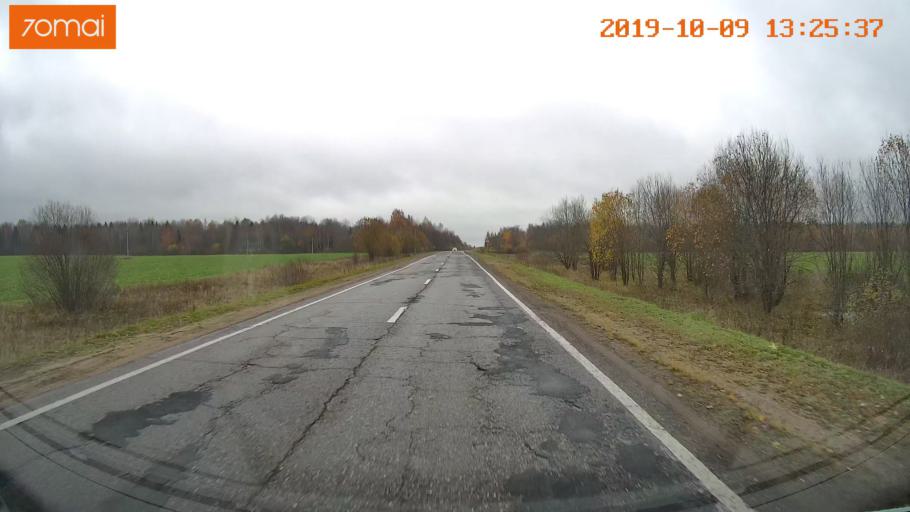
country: RU
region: Jaroslavl
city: Lyubim
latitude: 58.3269
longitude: 40.9136
